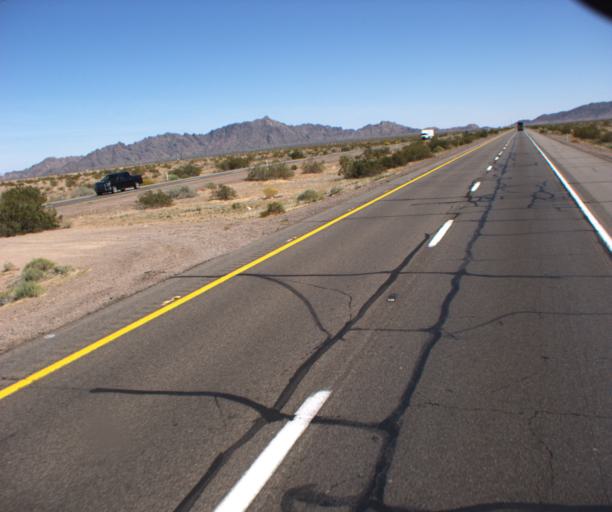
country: US
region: Arizona
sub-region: Yuma County
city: Wellton
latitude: 32.7114
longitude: -113.8348
